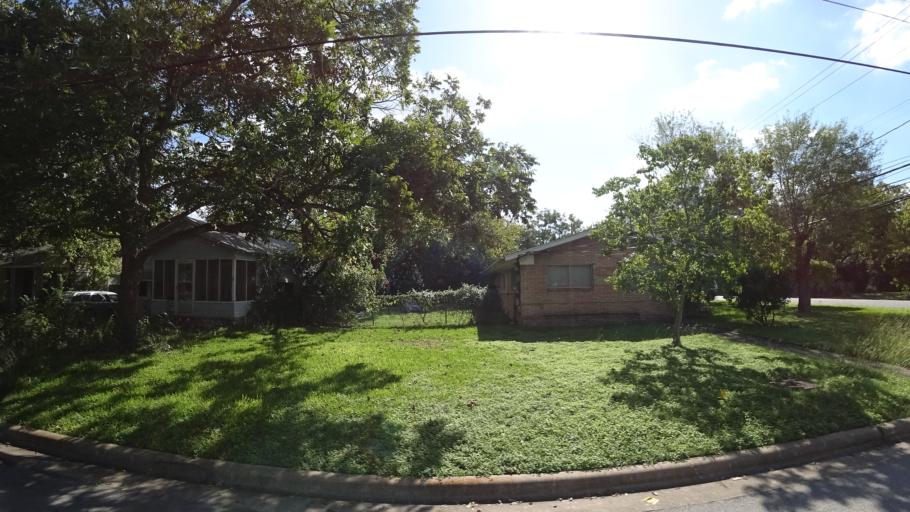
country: US
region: Texas
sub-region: Travis County
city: Austin
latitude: 30.3127
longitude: -97.7123
